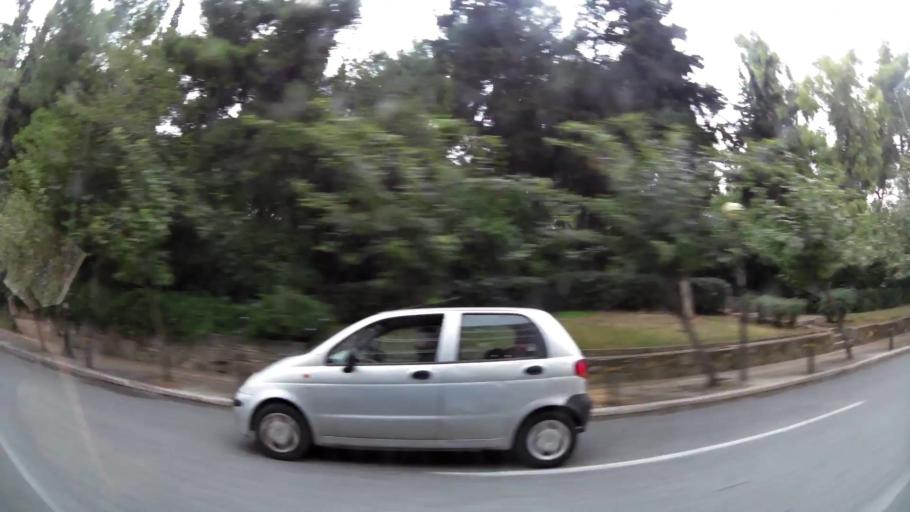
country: GR
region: Attica
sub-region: Nomarchia Athinas
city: Dhafni
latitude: 37.9630
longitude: 23.7338
